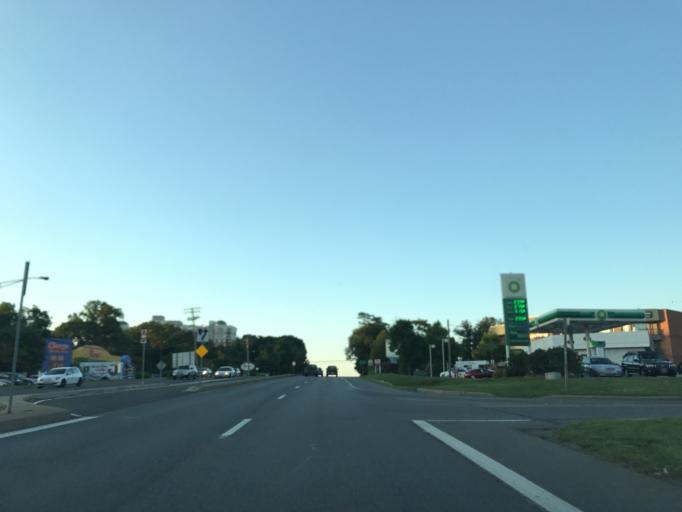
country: US
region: Maryland
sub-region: Anne Arundel County
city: Parole
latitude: 38.9756
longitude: -76.5408
